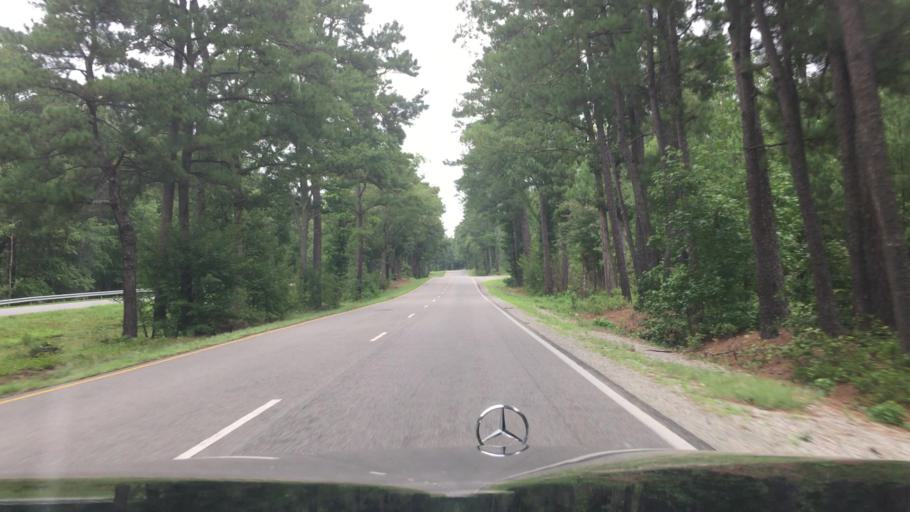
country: US
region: Virginia
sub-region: Chesterfield County
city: Woodlake
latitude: 37.3761
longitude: -77.8087
